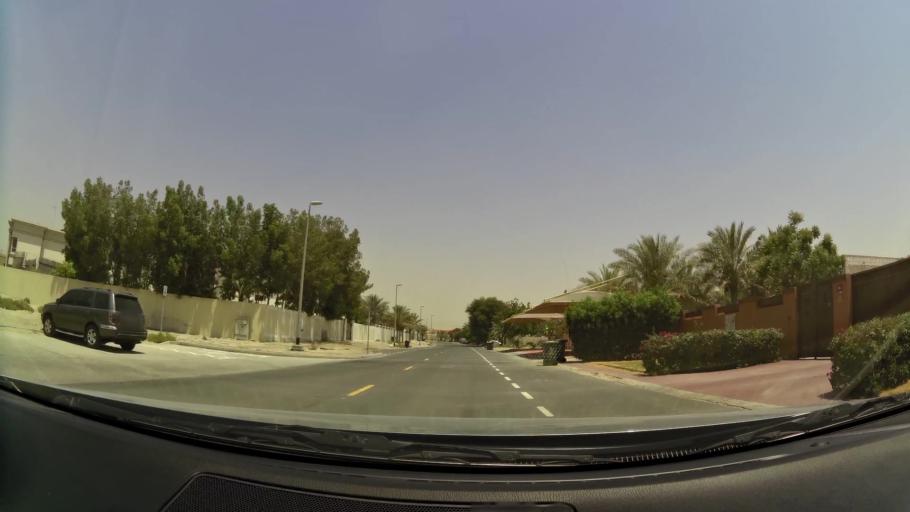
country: AE
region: Dubai
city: Dubai
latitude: 25.0862
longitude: 55.2001
